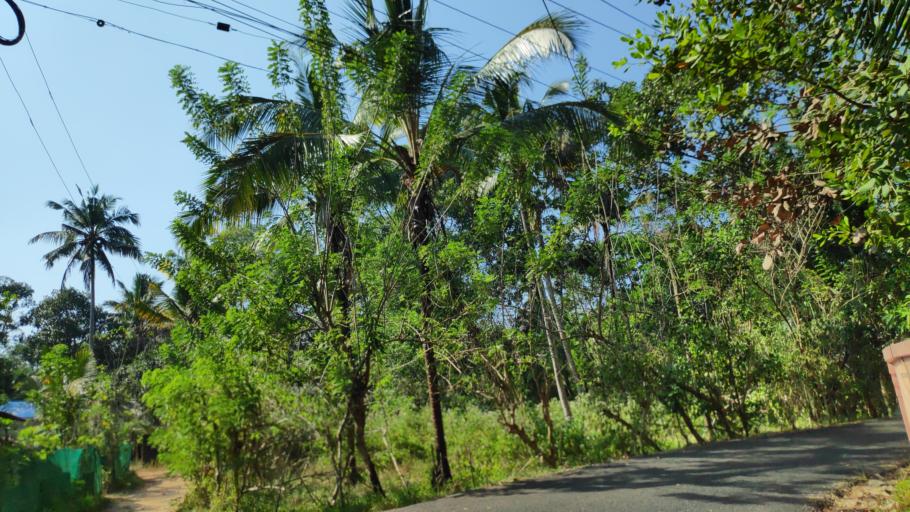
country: IN
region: Kerala
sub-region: Alappuzha
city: Alleppey
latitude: 9.5458
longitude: 76.3239
